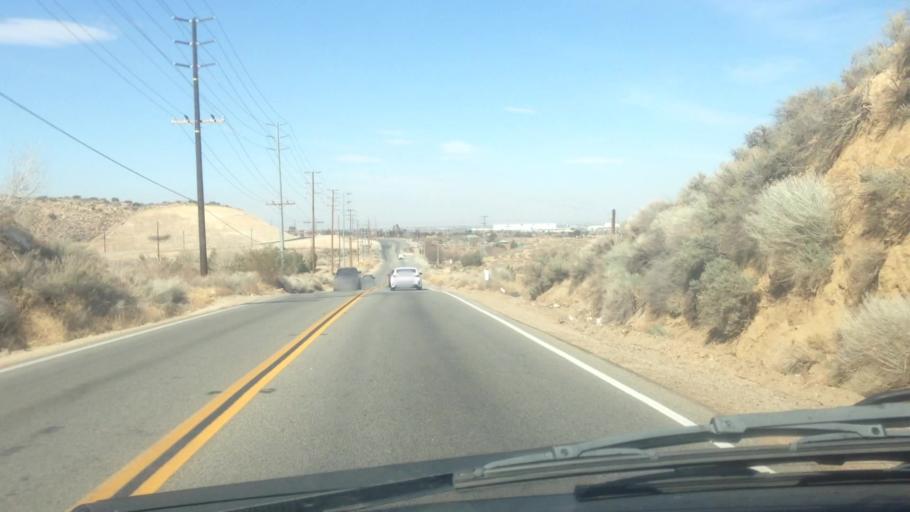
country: US
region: California
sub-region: Los Angeles County
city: Palmdale
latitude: 34.5621
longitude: -118.1408
